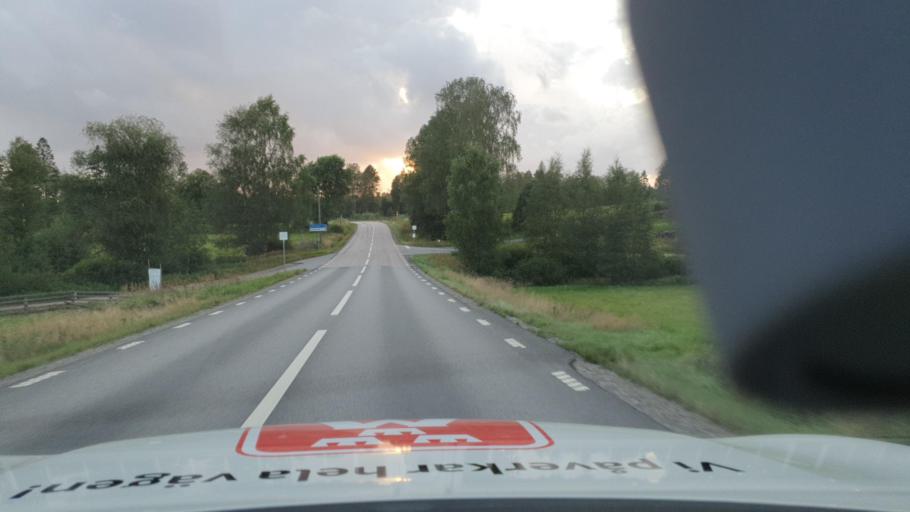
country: SE
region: Vaestra Goetaland
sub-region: Marks Kommun
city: Fritsla
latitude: 57.4937
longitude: 12.8636
